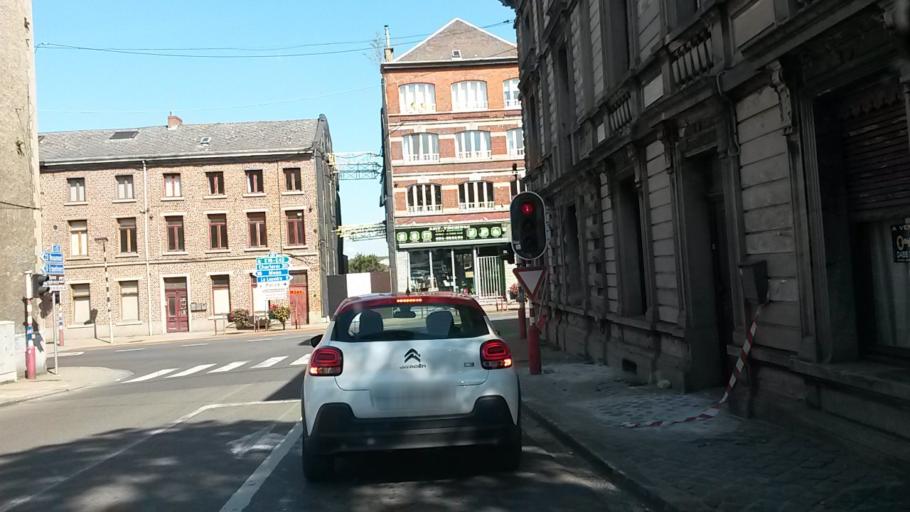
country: BE
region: Wallonia
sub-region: Province du Hainaut
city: Binche
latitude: 50.4116
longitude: 4.1710
